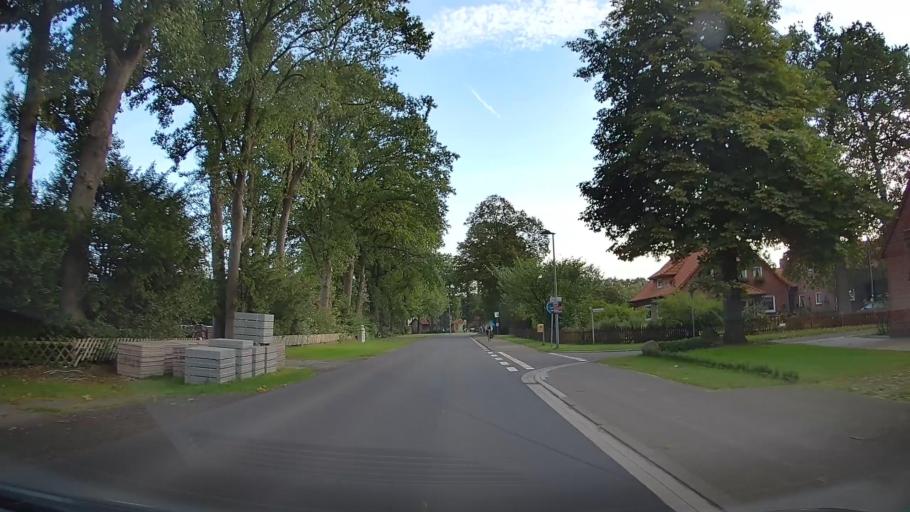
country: DE
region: Lower Saxony
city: Hassendorf
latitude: 53.1069
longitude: 9.2654
